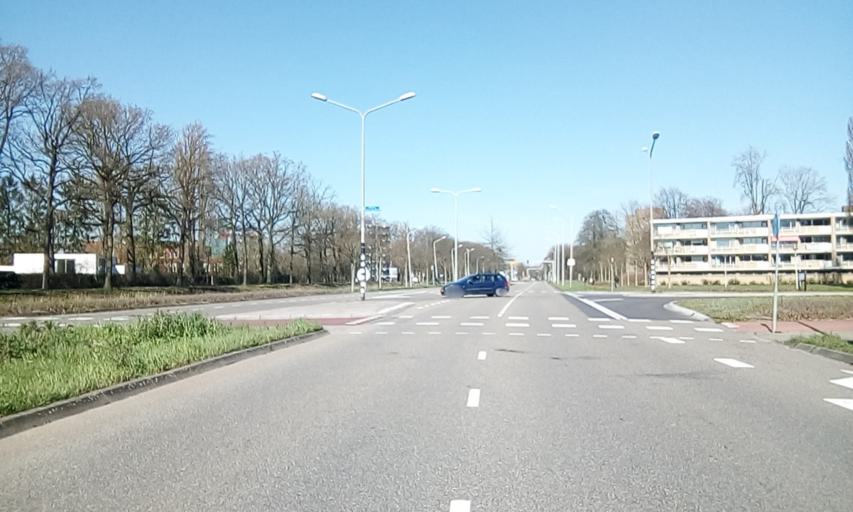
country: NL
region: Gelderland
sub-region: Gemeente Nijmegen
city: Lindenholt
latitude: 51.8082
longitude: 5.8033
